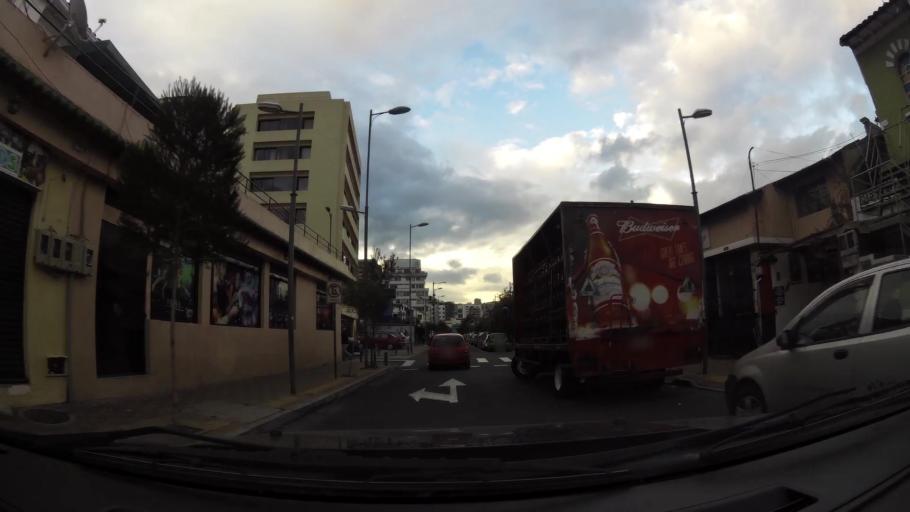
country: EC
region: Pichincha
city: Quito
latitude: -0.2037
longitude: -78.4907
